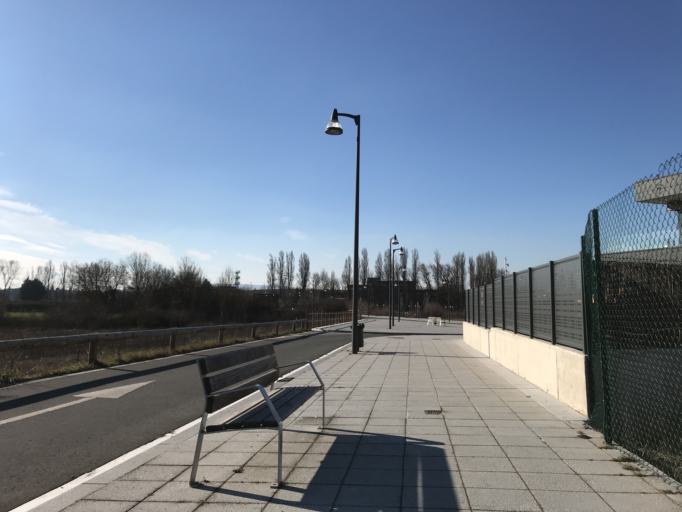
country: ES
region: Basque Country
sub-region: Provincia de Alava
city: Gasteiz / Vitoria
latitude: 42.8337
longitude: -2.6760
